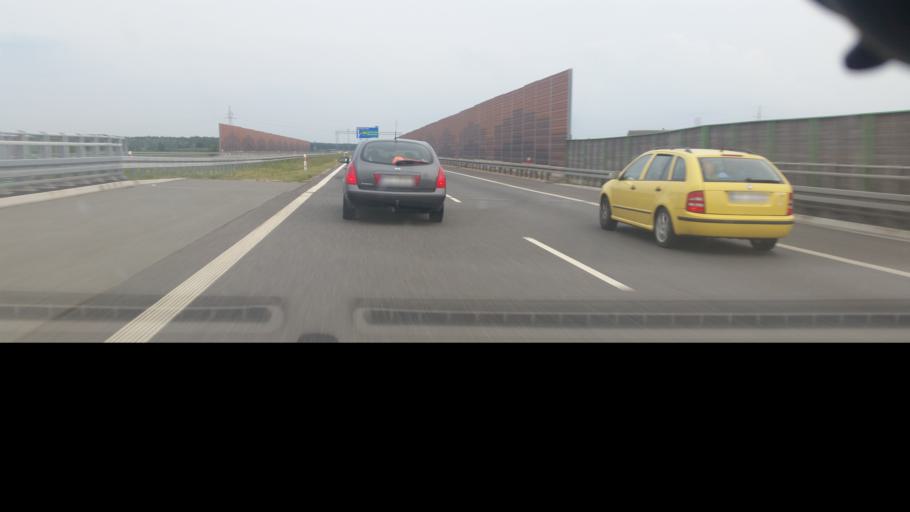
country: PL
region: Kujawsko-Pomorskie
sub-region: Powiat wloclawski
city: Lubanie
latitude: 52.7021
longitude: 18.8852
